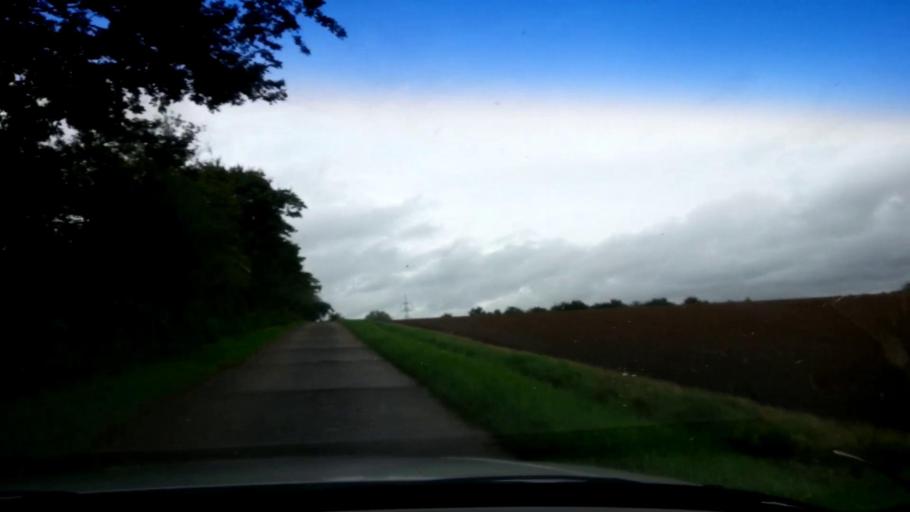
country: DE
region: Bavaria
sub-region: Upper Franconia
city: Memmelsdorf
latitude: 49.9521
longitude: 10.9798
